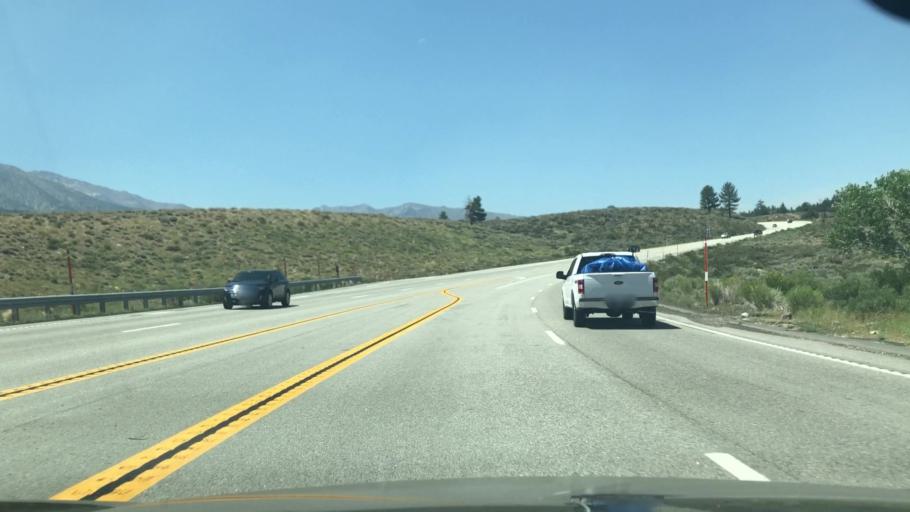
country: US
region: California
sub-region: Inyo County
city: West Bishop
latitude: 37.5583
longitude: -118.6586
